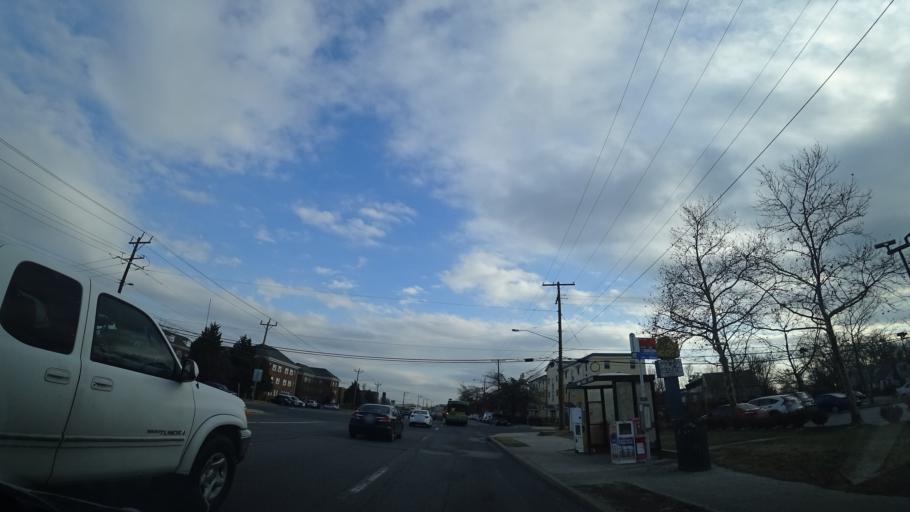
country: US
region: Maryland
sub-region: Prince George's County
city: Langley Park
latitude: 38.9930
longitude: -76.9919
